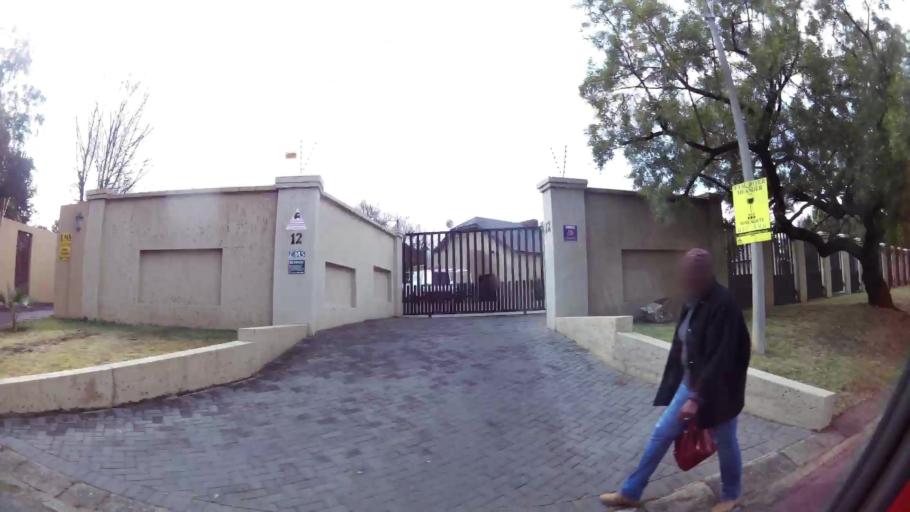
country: ZA
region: Gauteng
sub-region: Sedibeng District Municipality
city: Vanderbijlpark
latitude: -26.7423
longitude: 27.8266
